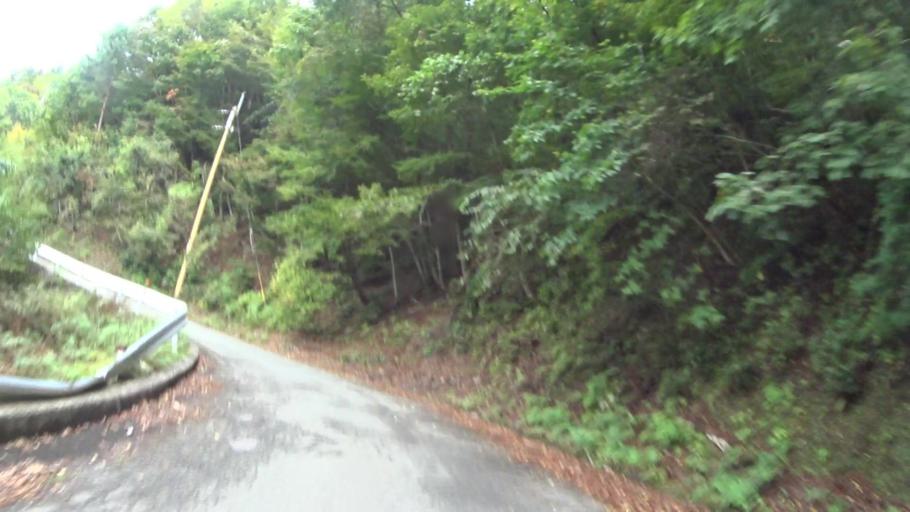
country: JP
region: Shiga Prefecture
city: Kitahama
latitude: 35.2708
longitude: 135.7374
